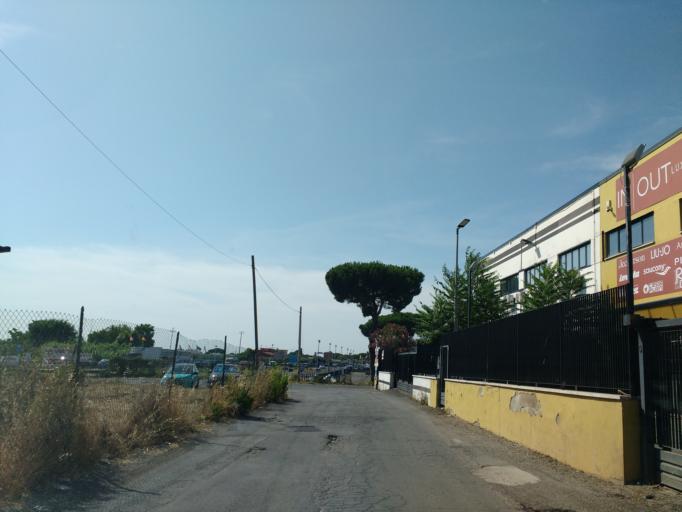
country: IT
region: Latium
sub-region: Citta metropolitana di Roma Capitale
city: Ciampino
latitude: 41.7808
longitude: 12.6042
